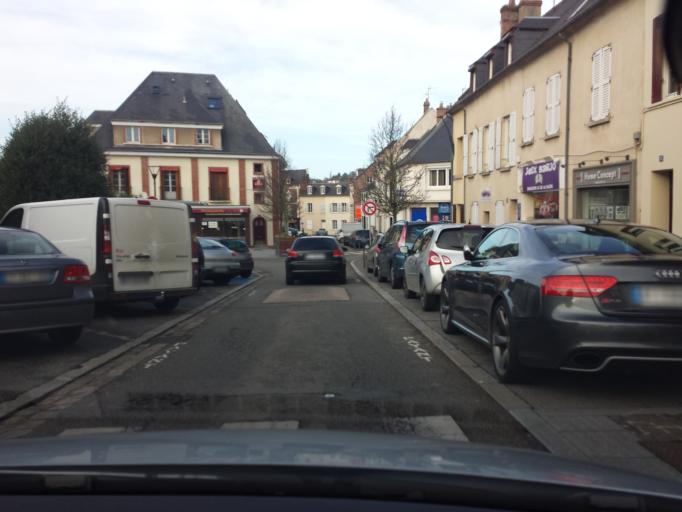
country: FR
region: Haute-Normandie
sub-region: Departement de l'Eure
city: Evreux
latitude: 49.0220
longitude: 1.1527
